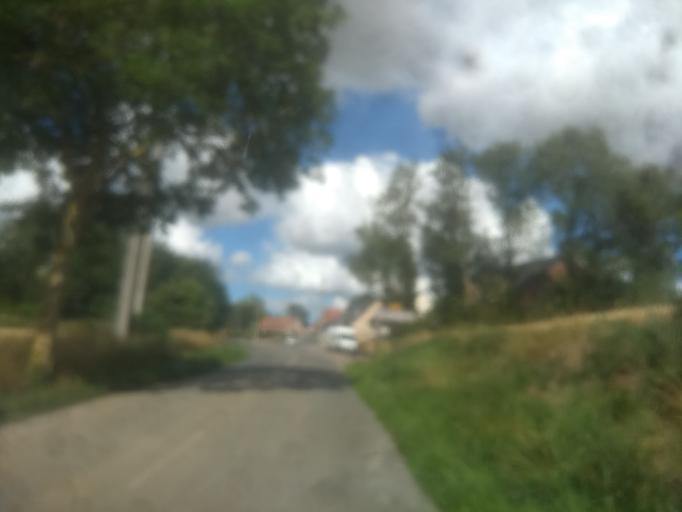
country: FR
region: Nord-Pas-de-Calais
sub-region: Departement du Pas-de-Calais
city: Achiet-le-Grand
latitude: 50.1864
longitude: 2.8042
